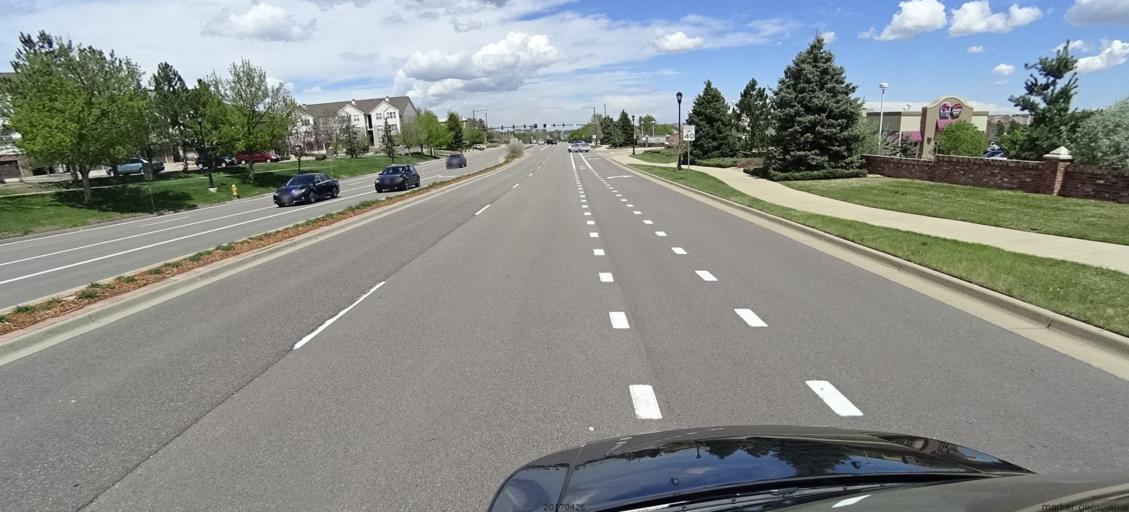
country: US
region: Colorado
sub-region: Adams County
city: Lone Tree
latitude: 39.5372
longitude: -104.8854
